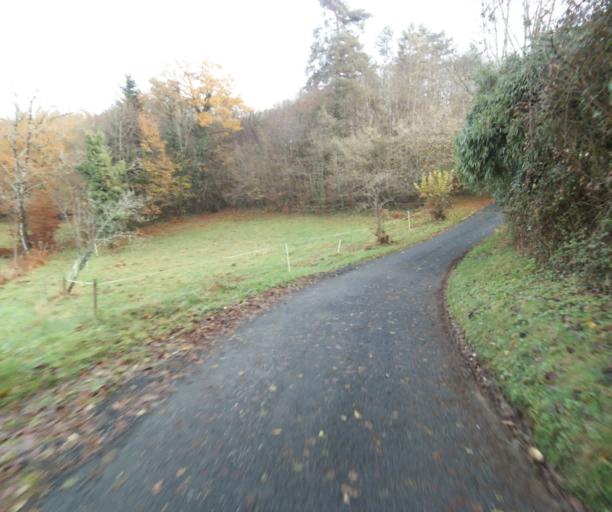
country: FR
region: Limousin
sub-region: Departement de la Correze
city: Cornil
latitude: 45.2034
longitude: 1.7011
